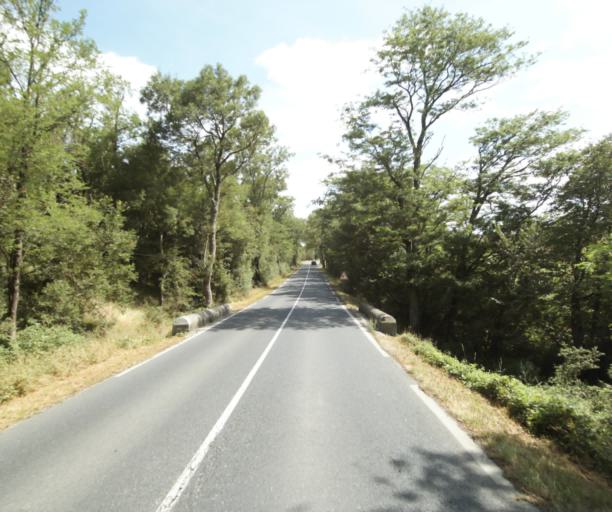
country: FR
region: Midi-Pyrenees
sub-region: Departement du Tarn
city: Dourgne
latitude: 43.4800
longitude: 2.1112
